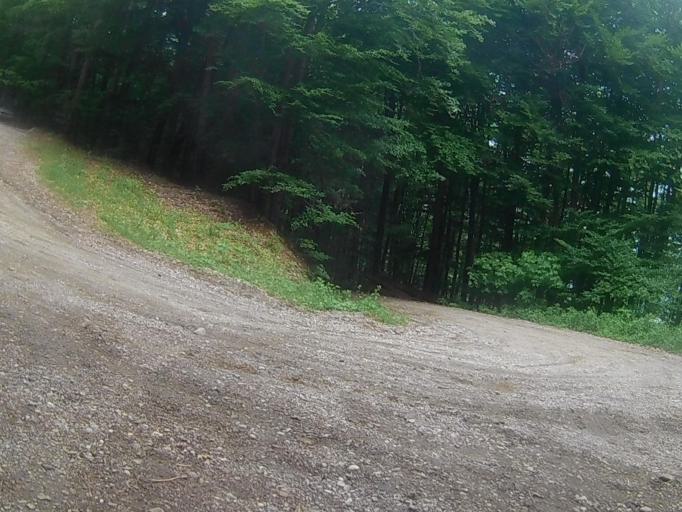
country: SI
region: Maribor
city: Pekre
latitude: 46.5227
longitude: 15.5825
